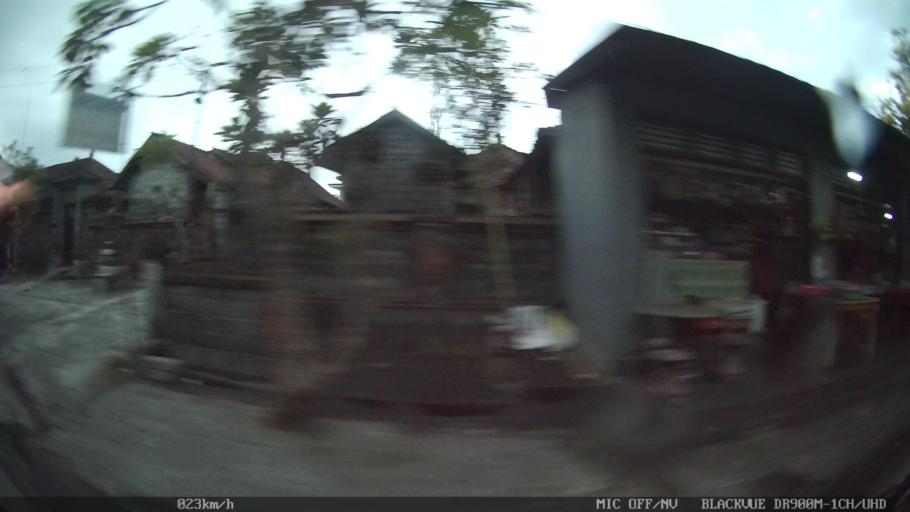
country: ID
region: Bali
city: Banjar Pasekan
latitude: -8.6234
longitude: 115.2743
